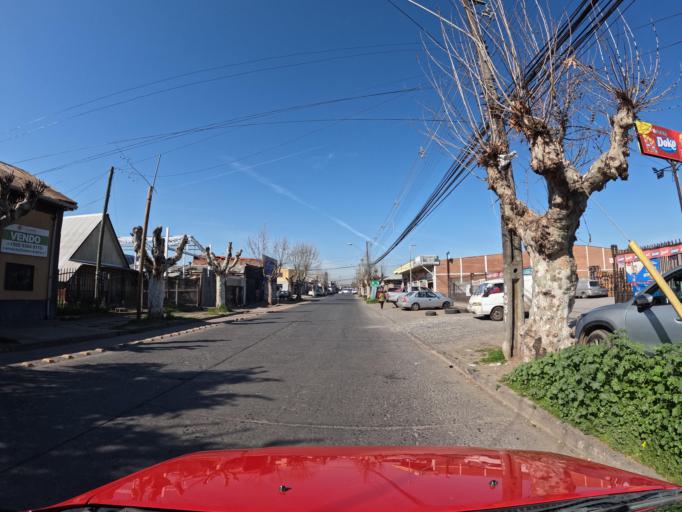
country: CL
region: Maule
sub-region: Provincia de Curico
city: Curico
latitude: -34.9799
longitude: -71.2449
